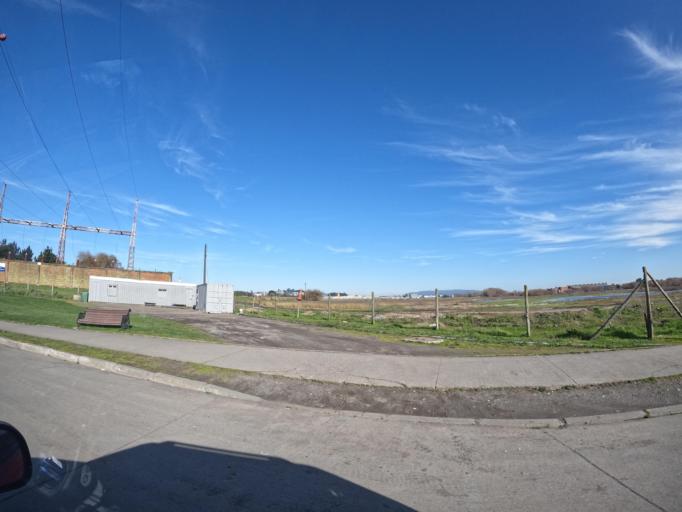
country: CL
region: Biobio
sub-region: Provincia de Concepcion
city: Concepcion
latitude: -36.7768
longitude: -73.0709
